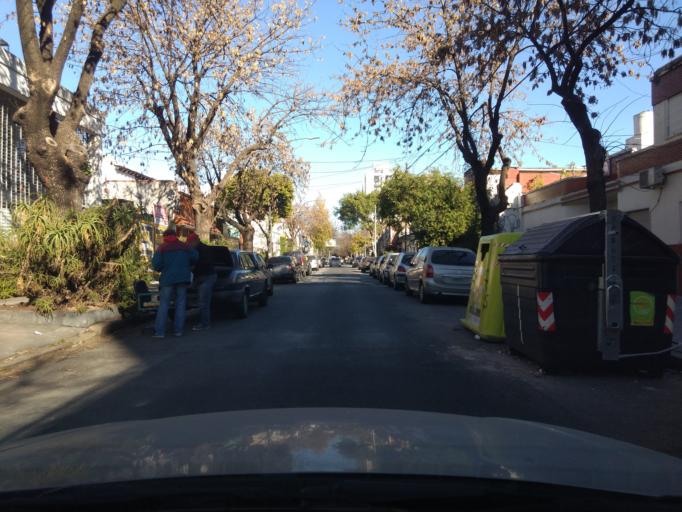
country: AR
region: Buenos Aires F.D.
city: Villa Santa Rita
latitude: -34.6130
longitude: -58.4736
